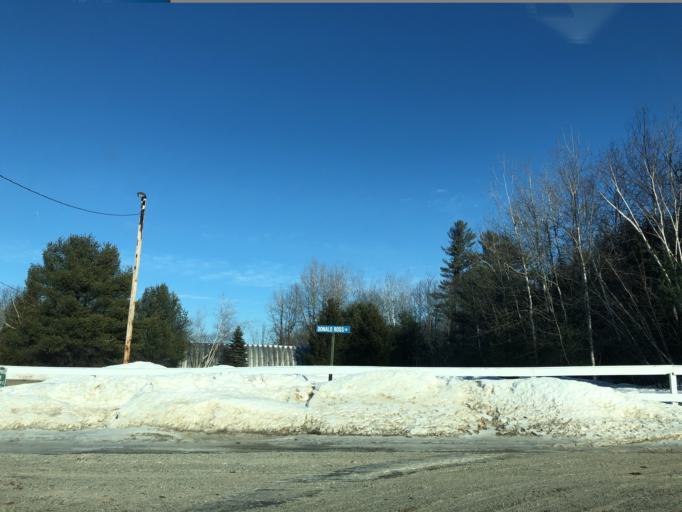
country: US
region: Maine
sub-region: Androscoggin County
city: Poland
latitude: 44.0281
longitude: -70.3614
